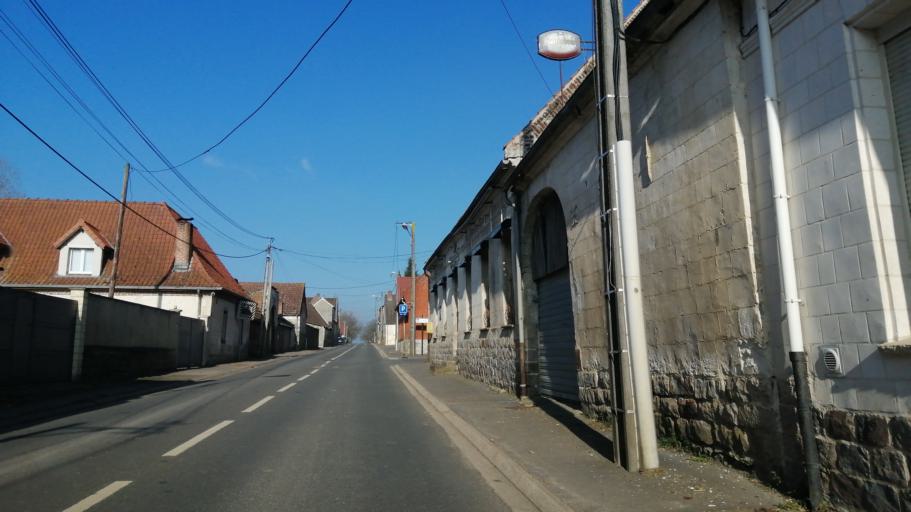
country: FR
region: Nord-Pas-de-Calais
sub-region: Departement du Pas-de-Calais
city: Aubigny-en-Artois
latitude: 50.3978
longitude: 2.6088
